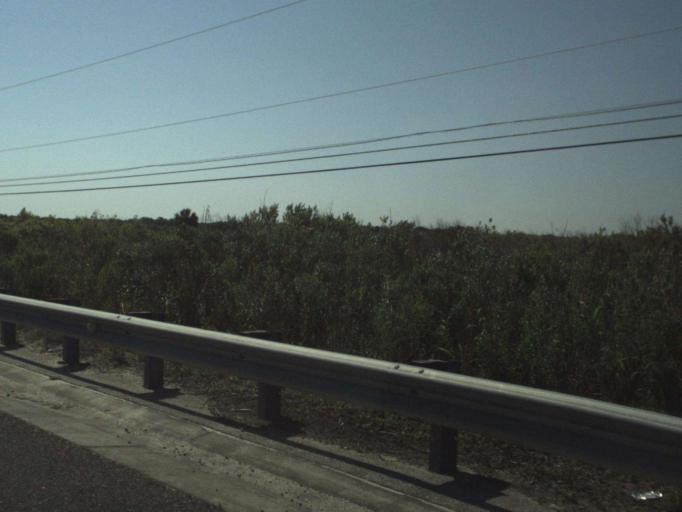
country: US
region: Florida
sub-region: Brevard County
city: Cocoa West
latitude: 28.3691
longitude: -80.8681
